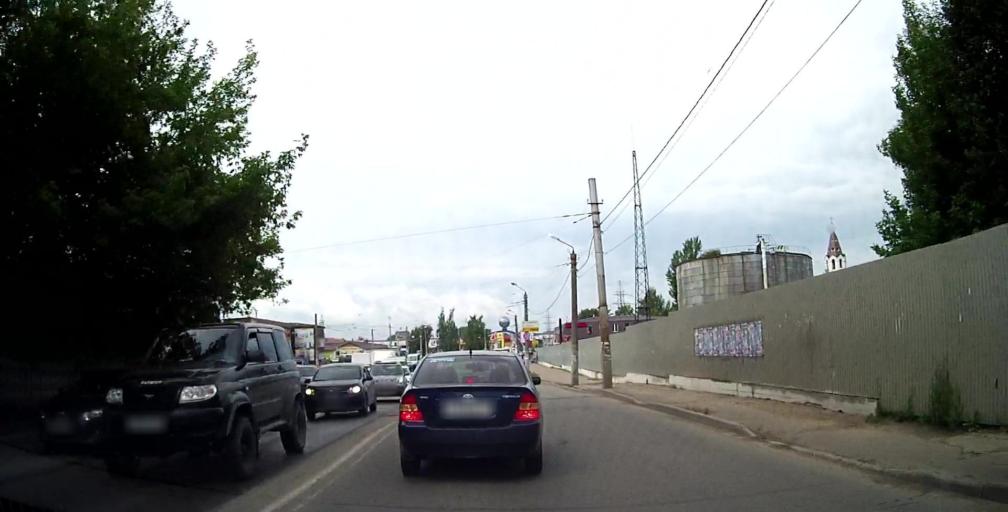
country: RU
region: Smolensk
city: Smolensk
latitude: 54.7948
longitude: 32.0411
